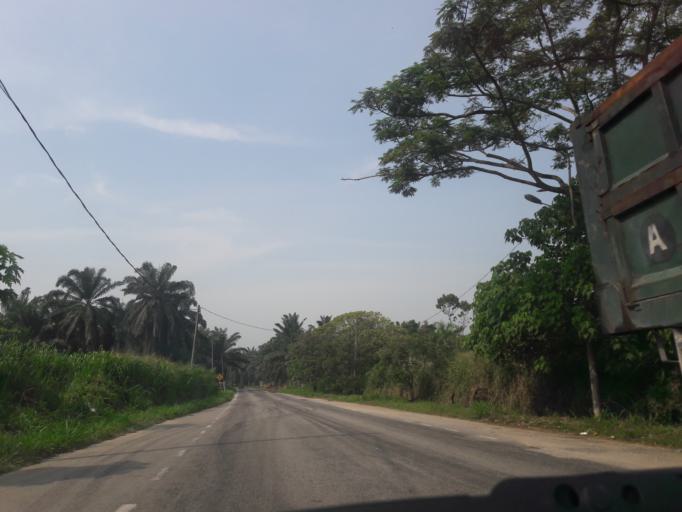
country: MY
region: Kedah
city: Kulim
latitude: 5.3500
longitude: 100.5197
